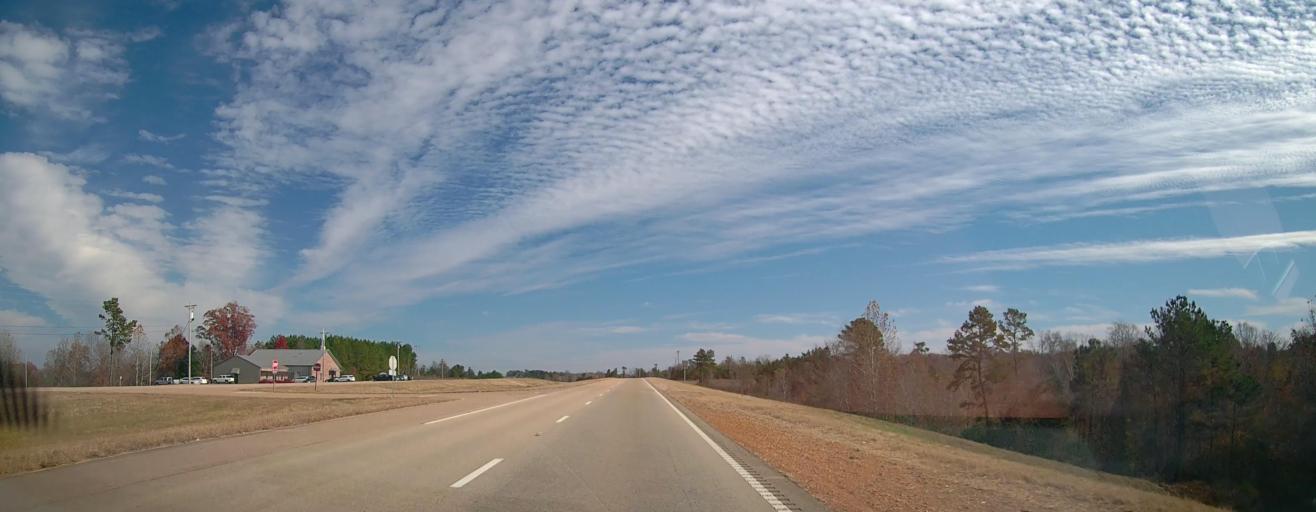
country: US
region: Mississippi
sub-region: Benton County
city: Ashland
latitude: 34.9532
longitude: -89.0107
